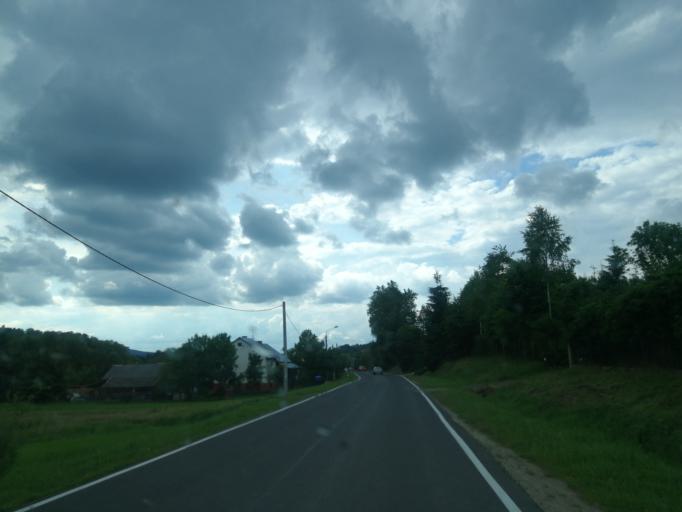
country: PL
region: Subcarpathian Voivodeship
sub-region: Powiat leski
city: Olszanica
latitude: 49.4487
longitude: 22.4415
